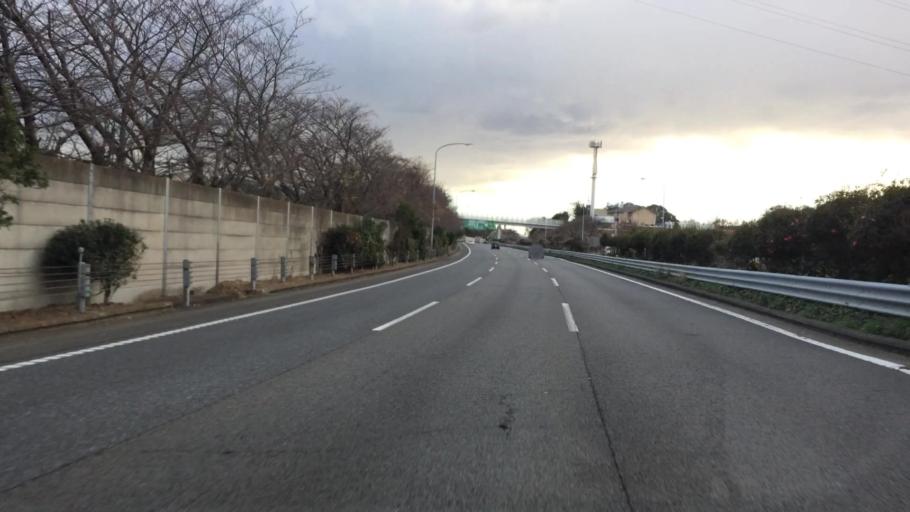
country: JP
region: Kanagawa
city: Yokohama
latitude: 35.4972
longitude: 139.5915
